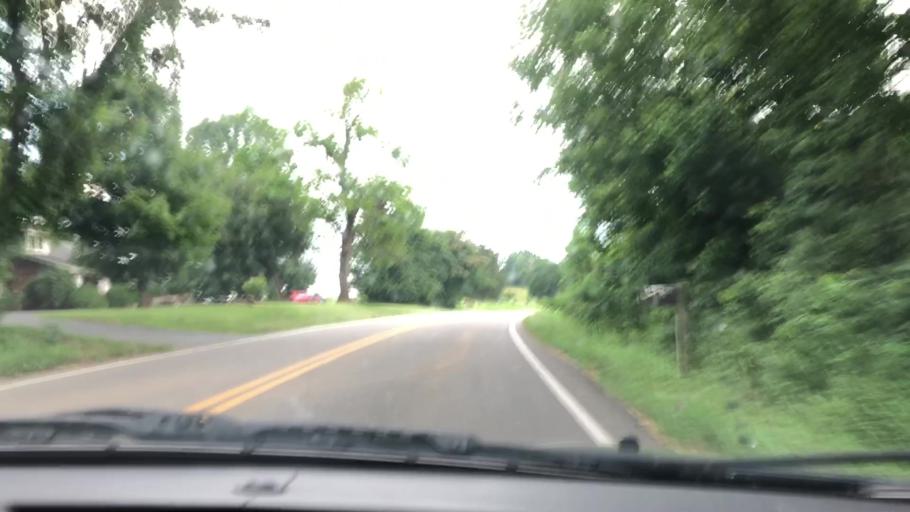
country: US
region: Tennessee
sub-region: Maury County
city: Columbia
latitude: 35.6868
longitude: -87.0111
